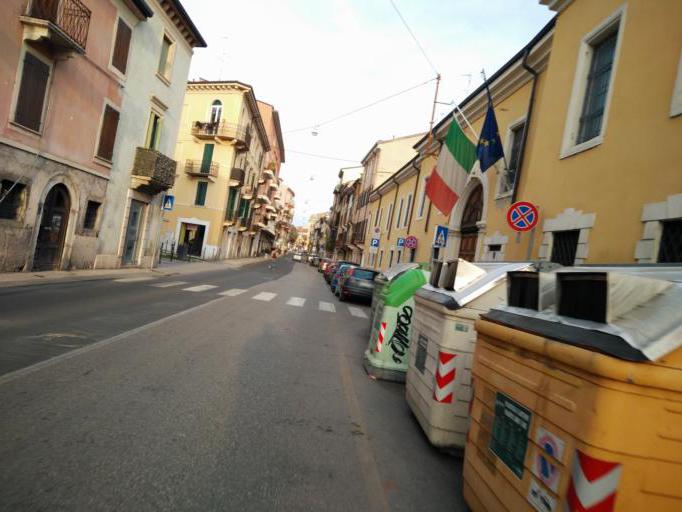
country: IT
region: Veneto
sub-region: Provincia di Verona
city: Verona
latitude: 45.4397
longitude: 11.0098
